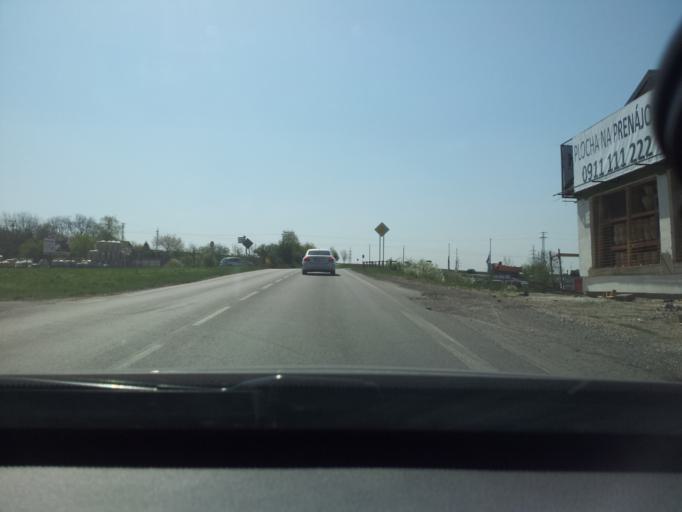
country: SK
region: Nitriansky
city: Banovce nad Bebravou
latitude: 48.7122
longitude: 18.2555
